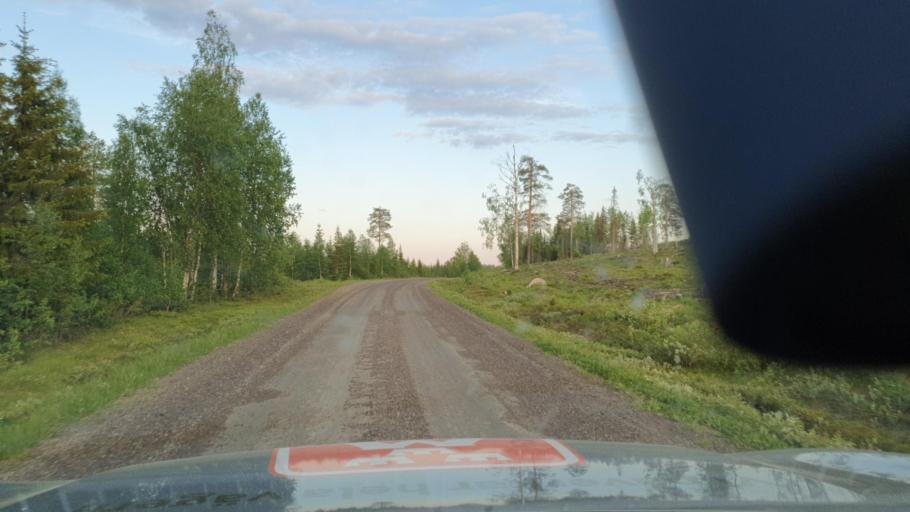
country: SE
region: Norrbotten
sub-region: Bodens Kommun
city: Boden
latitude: 66.4747
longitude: 21.6236
